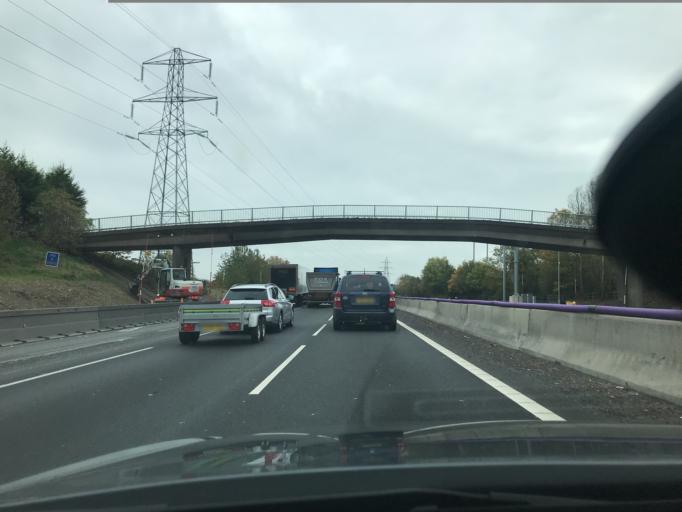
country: GB
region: England
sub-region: Cheshire East
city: Knutsford
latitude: 53.2636
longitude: -2.4017
